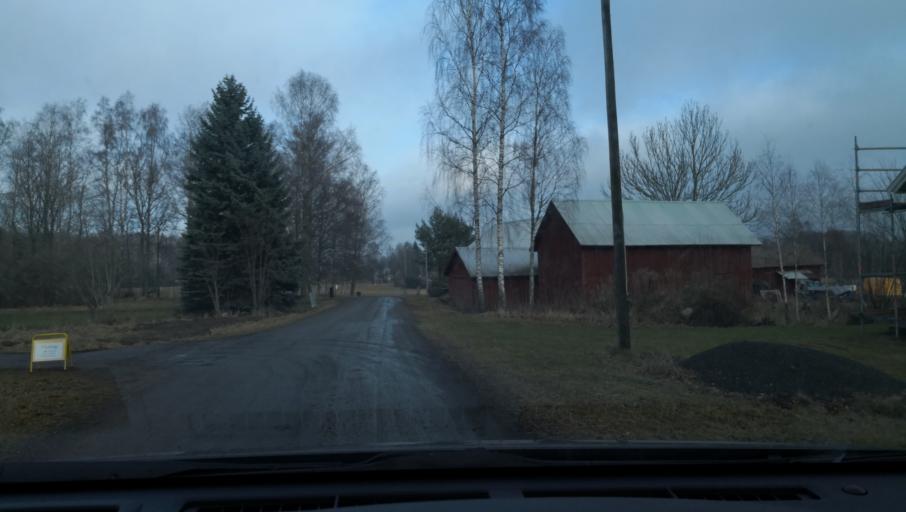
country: SE
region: Vaestra Goetaland
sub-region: Gullspangs Kommun
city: Gullspang
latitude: 58.9626
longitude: 14.0944
